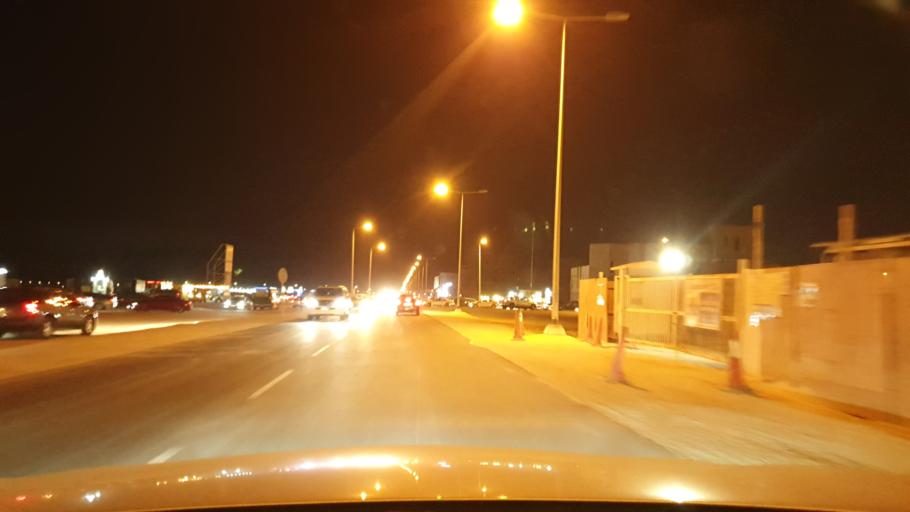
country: BH
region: Muharraq
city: Al Muharraq
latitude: 26.2658
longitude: 50.5945
